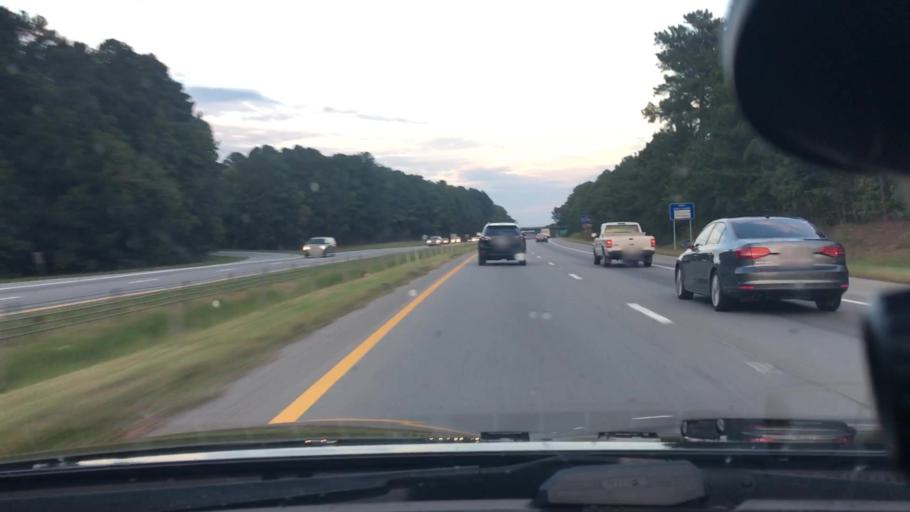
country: US
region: North Carolina
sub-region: Wake County
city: Apex
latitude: 35.7222
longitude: -78.8283
